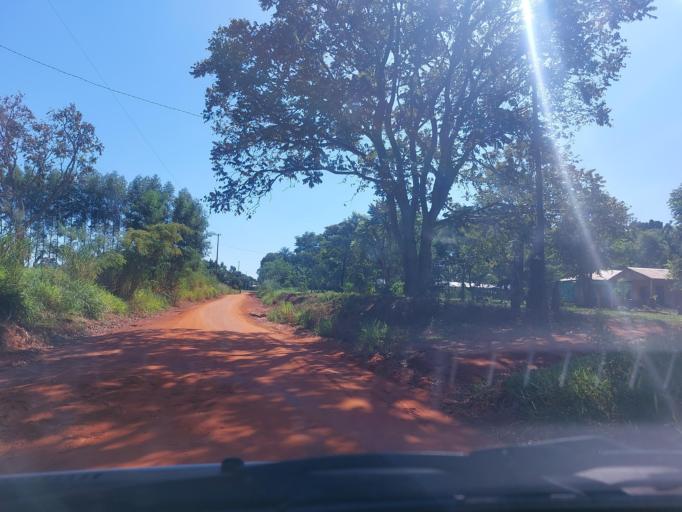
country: PY
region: San Pedro
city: Lima
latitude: -24.1645
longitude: -56.0134
